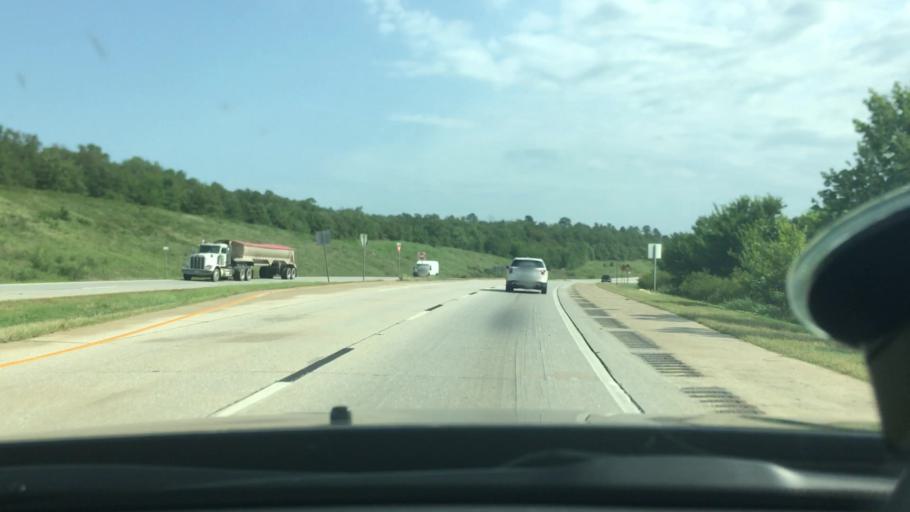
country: US
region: Oklahoma
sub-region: Atoka County
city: Atoka
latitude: 34.4520
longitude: -96.0705
